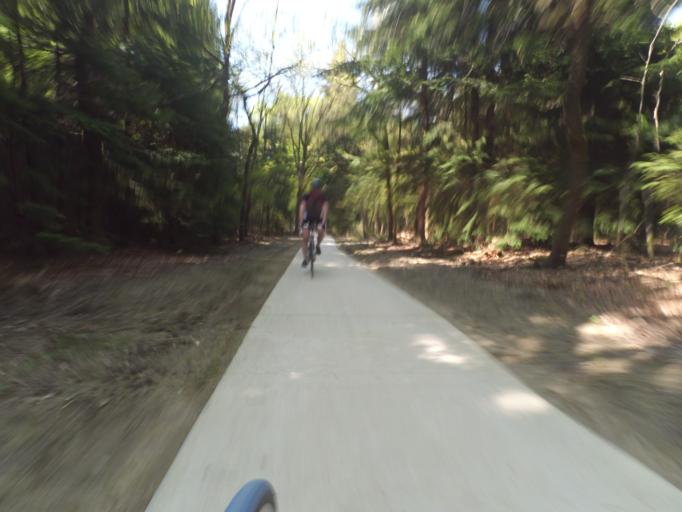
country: NL
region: Gelderland
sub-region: Gemeente Apeldoorn
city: Apeldoorn
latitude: 52.2153
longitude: 5.9034
